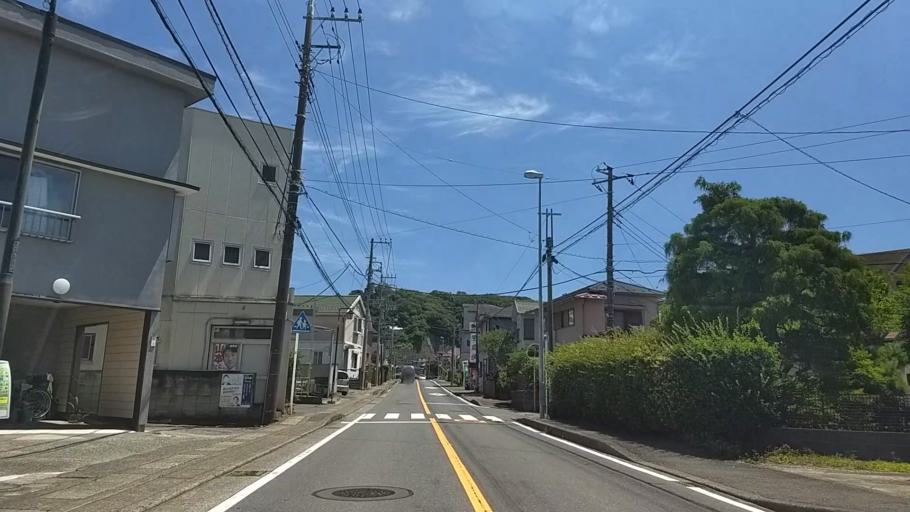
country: JP
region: Kanagawa
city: Kamakura
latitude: 35.3118
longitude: 139.5572
